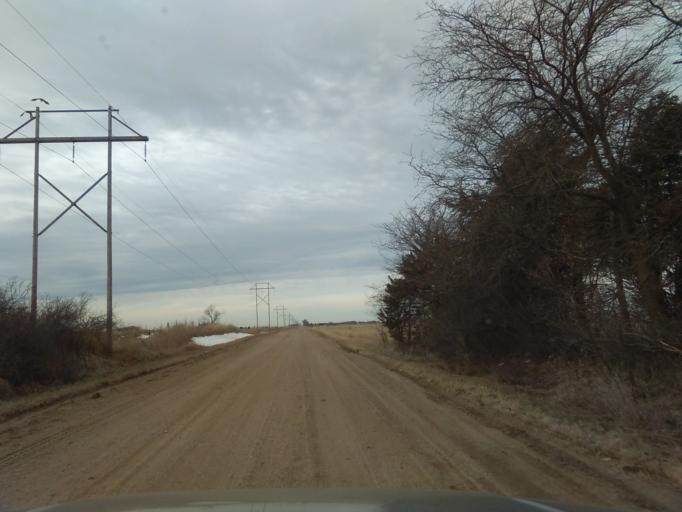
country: US
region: Nebraska
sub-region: Buffalo County
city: Shelton
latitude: 40.6548
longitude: -98.7299
